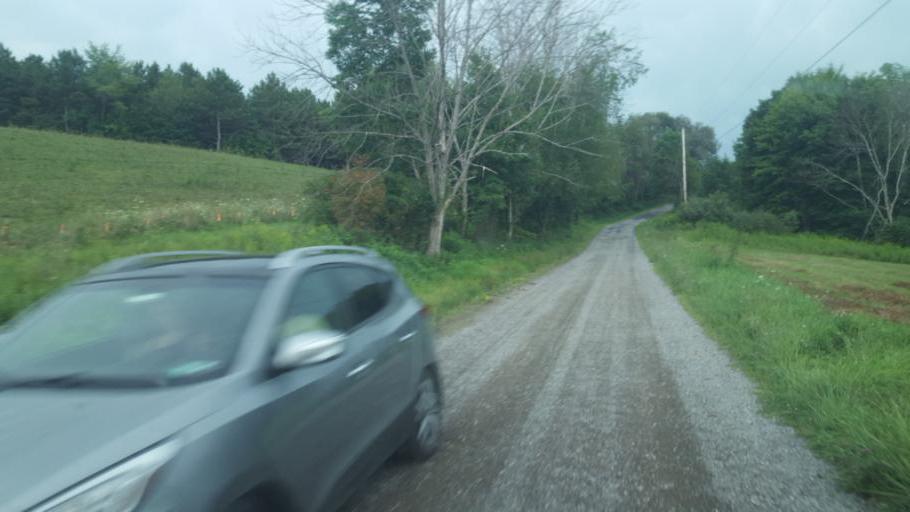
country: US
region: Pennsylvania
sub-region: Clarion County
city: Knox
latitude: 41.1484
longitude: -79.5171
